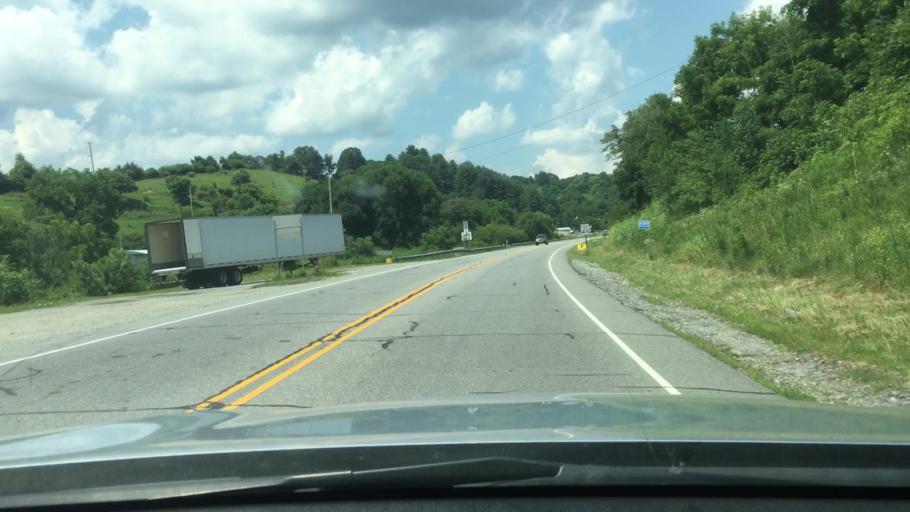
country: US
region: North Carolina
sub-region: Madison County
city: Marshall
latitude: 35.8049
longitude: -82.6583
